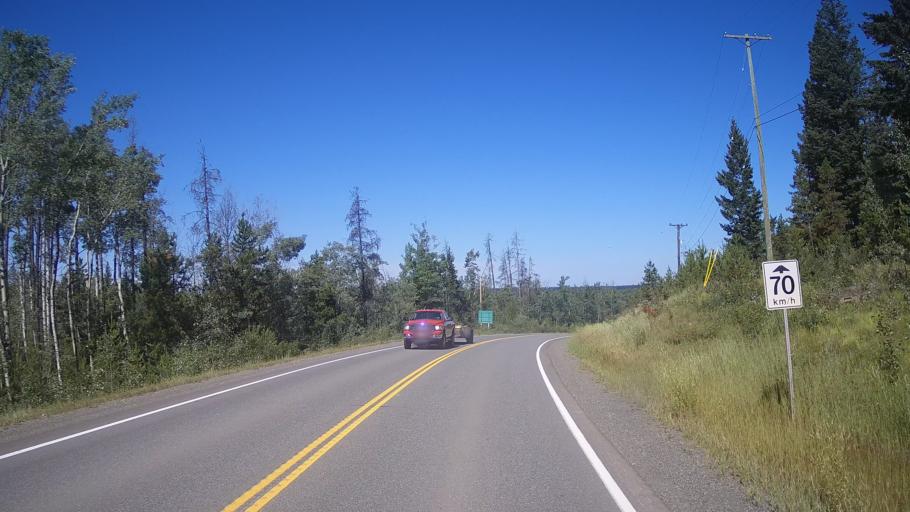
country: CA
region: British Columbia
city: Cache Creek
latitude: 51.5525
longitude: -121.1894
